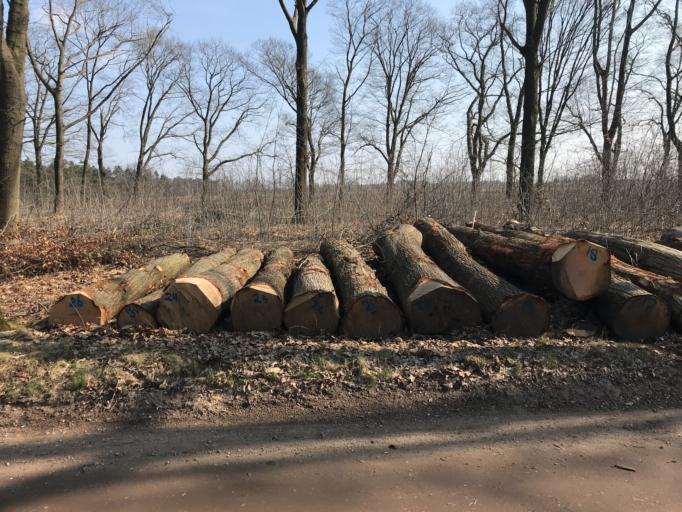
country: NL
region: Gelderland
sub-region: Gemeente Renkum
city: Renkum
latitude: 51.9948
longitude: 5.7372
